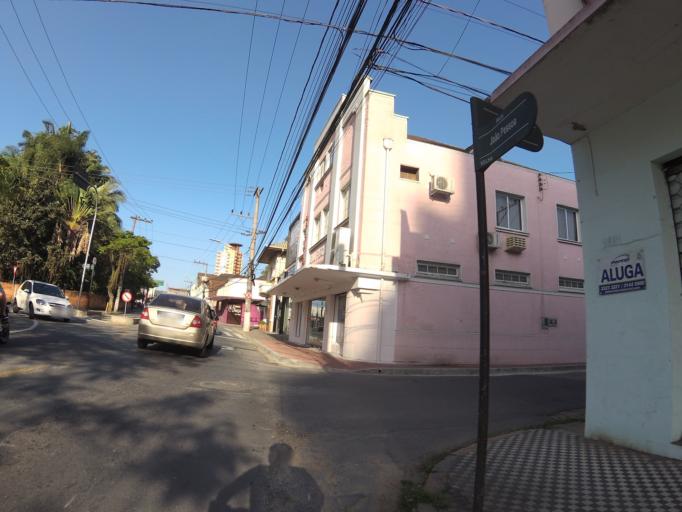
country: BR
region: Santa Catarina
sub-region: Blumenau
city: Blumenau
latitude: -26.9190
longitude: -49.0901
